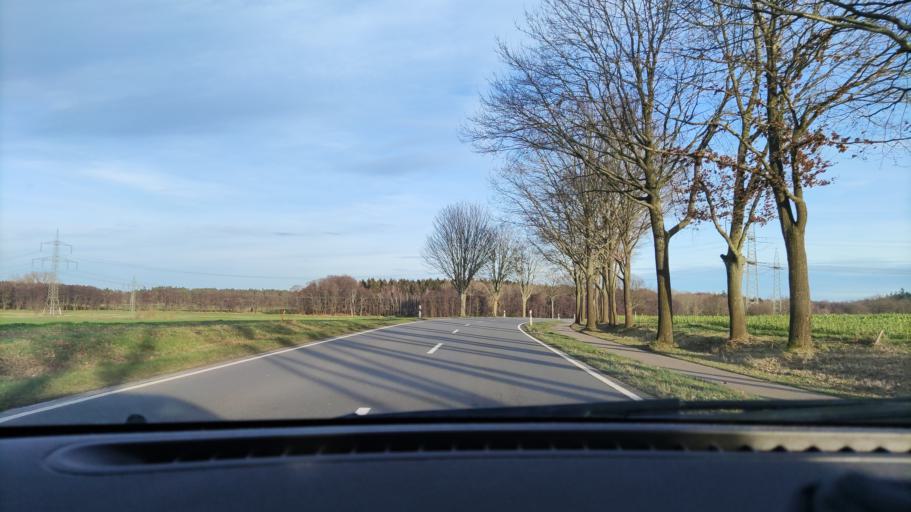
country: DE
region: Lower Saxony
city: Hanstedt Eins
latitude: 53.0385
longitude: 10.3875
